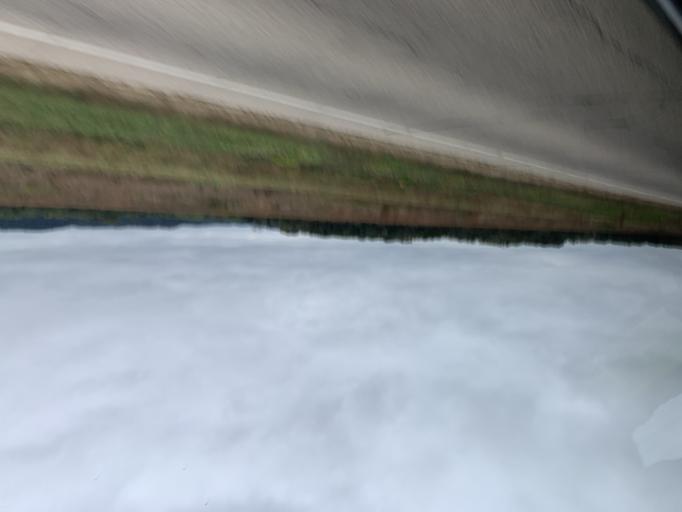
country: US
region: Wisconsin
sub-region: Grant County
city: Boscobel
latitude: 43.2054
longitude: -90.5940
